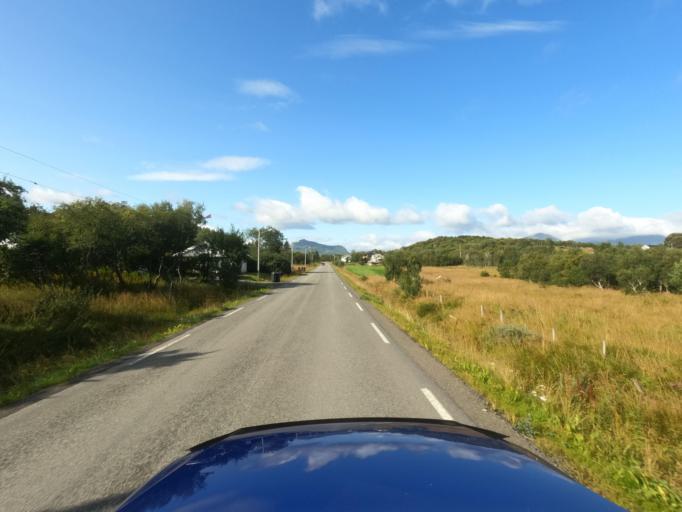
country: NO
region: Nordland
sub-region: Vestvagoy
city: Leknes
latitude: 68.1238
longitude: 13.6441
